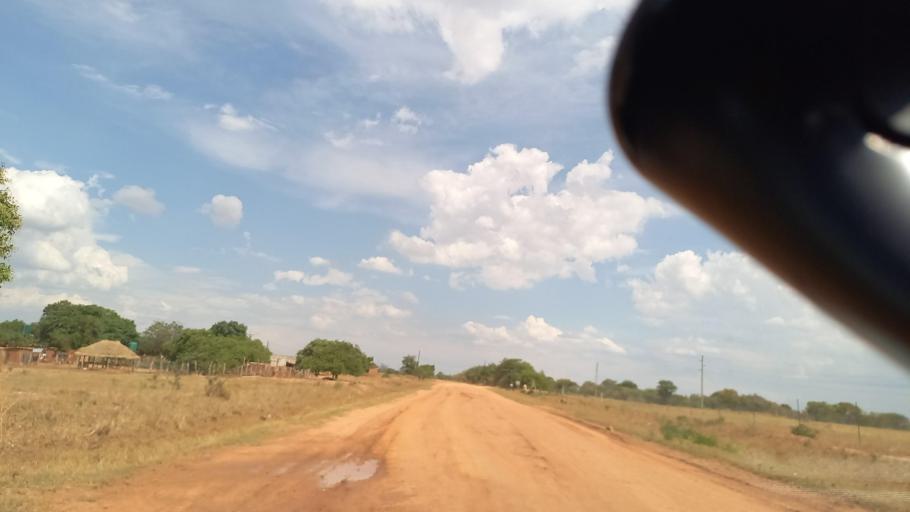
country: ZM
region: Lusaka
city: Kafue
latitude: -16.1147
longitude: 28.0320
